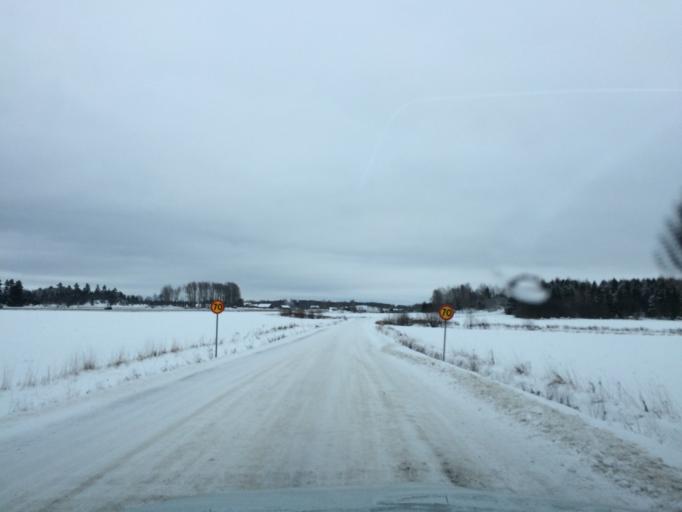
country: SE
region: Vaestmanland
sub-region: Hallstahammars Kommun
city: Kolback
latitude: 59.5902
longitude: 16.2502
